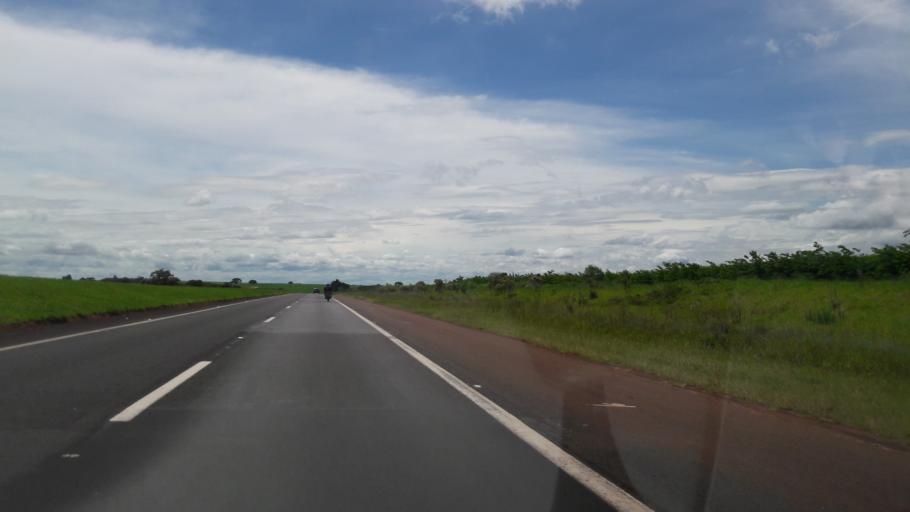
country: BR
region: Sao Paulo
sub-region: Avare
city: Avare
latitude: -22.9439
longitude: -48.8992
